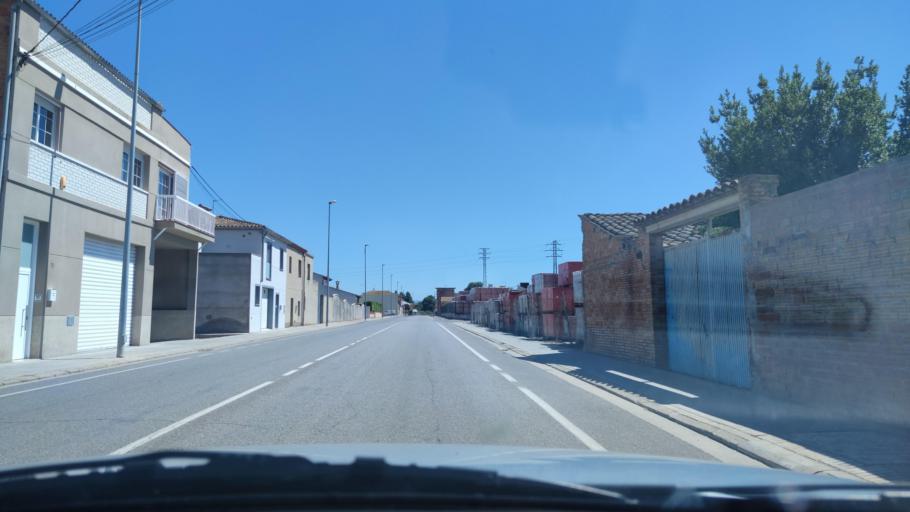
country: ES
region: Catalonia
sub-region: Provincia de Lleida
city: Mollerussa
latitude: 41.6344
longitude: 0.8761
